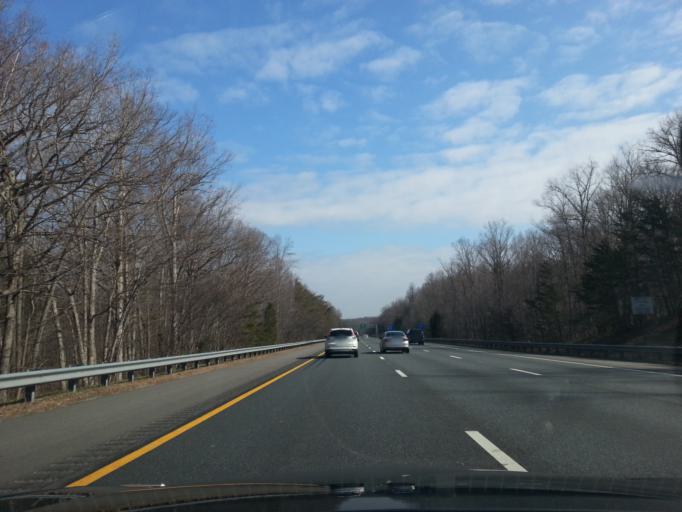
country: US
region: Virginia
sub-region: Stafford County
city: Stafford
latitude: 38.4367
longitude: -77.4127
